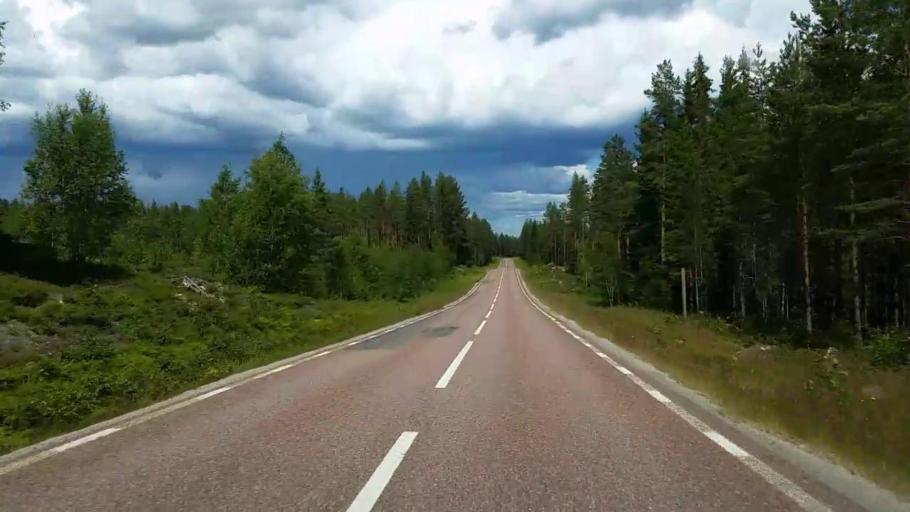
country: SE
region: Gaevleborg
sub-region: Ovanakers Kommun
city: Edsbyn
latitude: 61.3155
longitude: 15.5088
